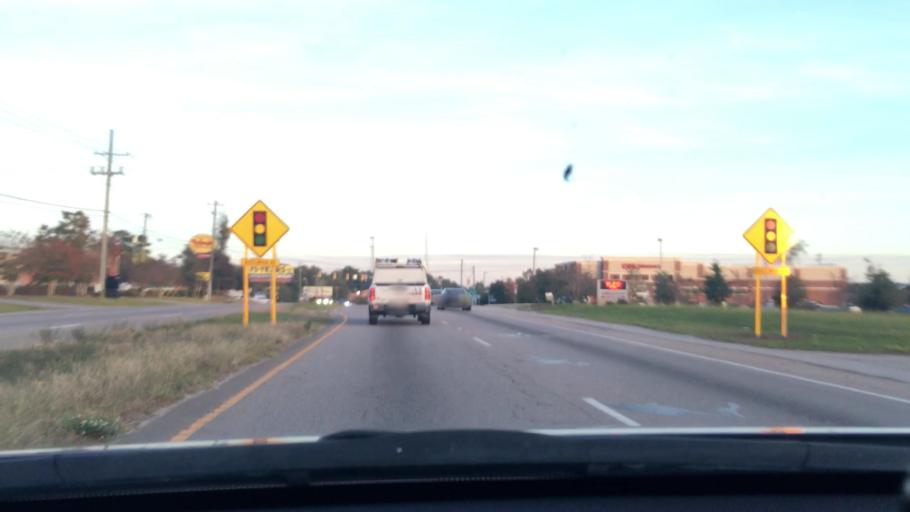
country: US
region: South Carolina
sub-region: Richland County
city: Hopkins
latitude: 33.9568
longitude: -80.9324
